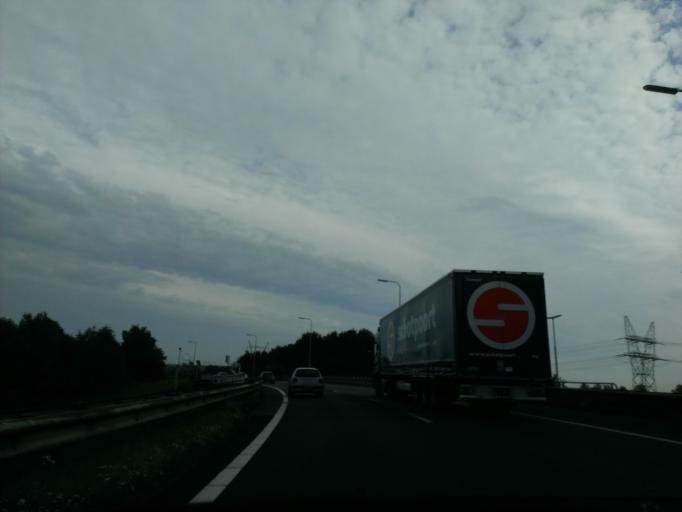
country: NL
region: Gelderland
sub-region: Gemeente Hattem
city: Hattem
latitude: 52.4854
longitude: 6.0205
